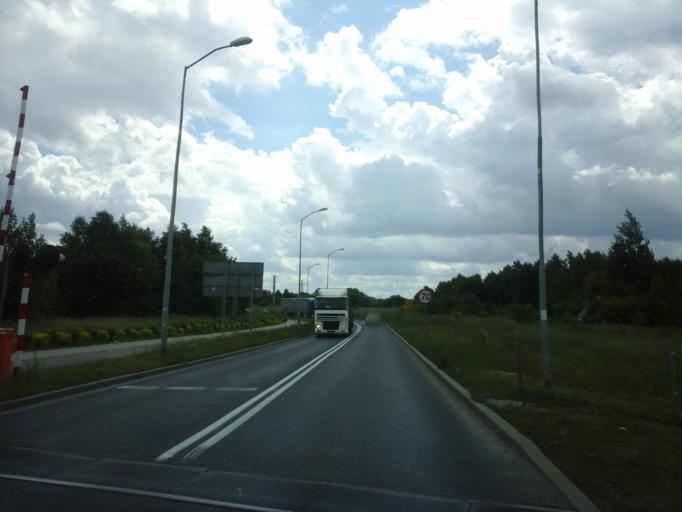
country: PL
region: West Pomeranian Voivodeship
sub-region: Koszalin
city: Koszalin
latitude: 54.1821
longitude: 16.1522
